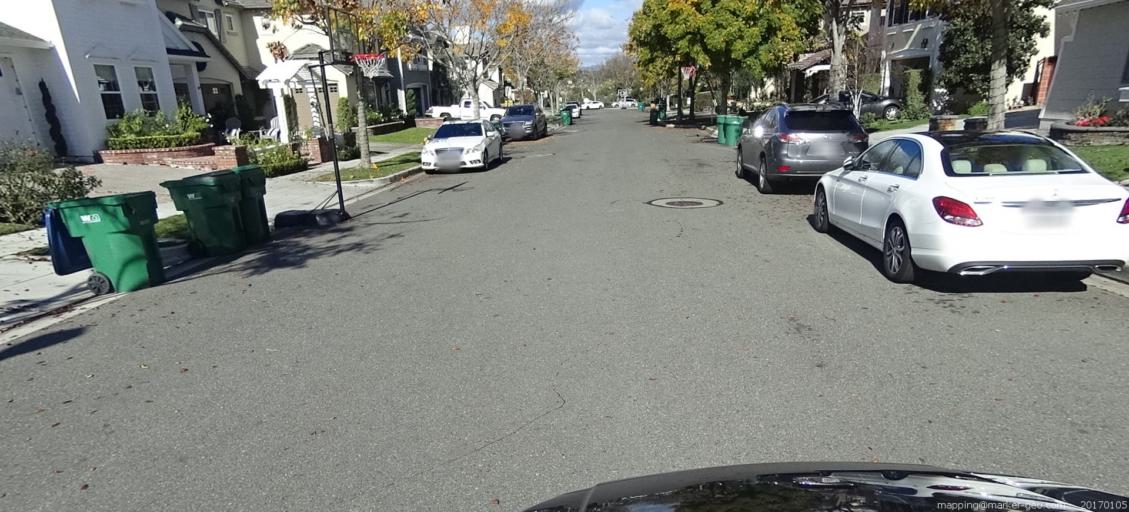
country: US
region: California
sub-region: Orange County
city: Ladera Ranch
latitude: 33.5461
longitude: -117.6324
